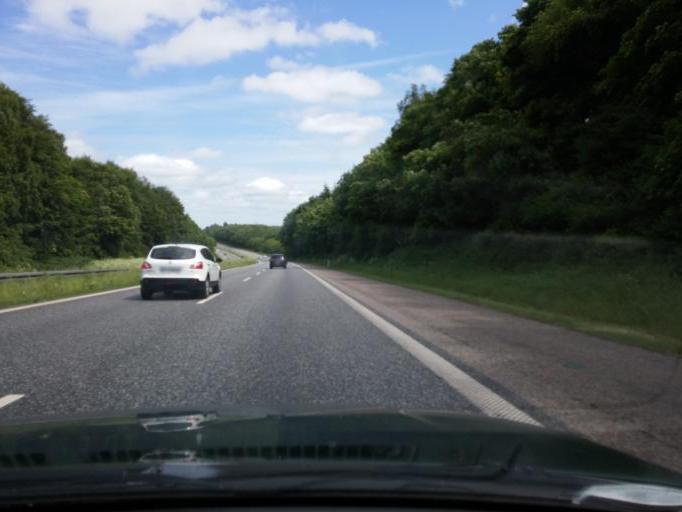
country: DK
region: South Denmark
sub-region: Fredericia Kommune
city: Taulov
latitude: 55.5457
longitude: 9.5429
